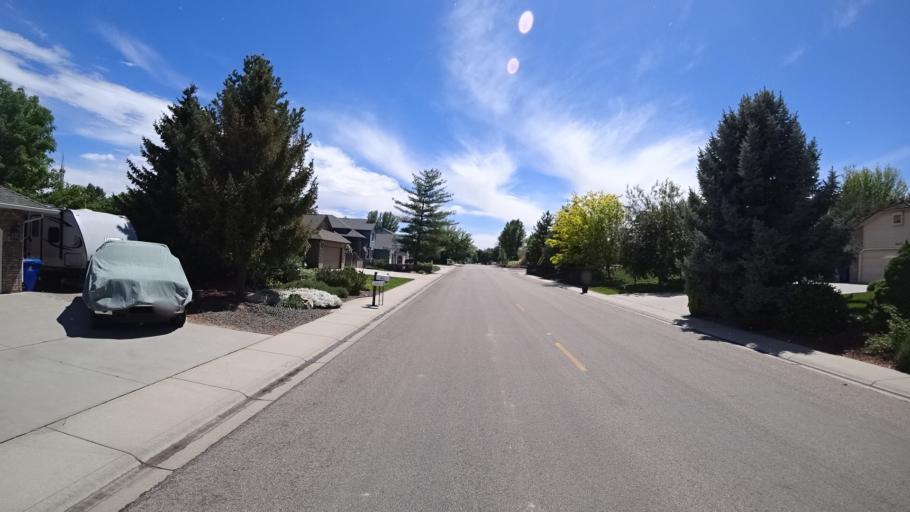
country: US
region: Idaho
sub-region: Ada County
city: Meridian
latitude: 43.5697
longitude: -116.3250
